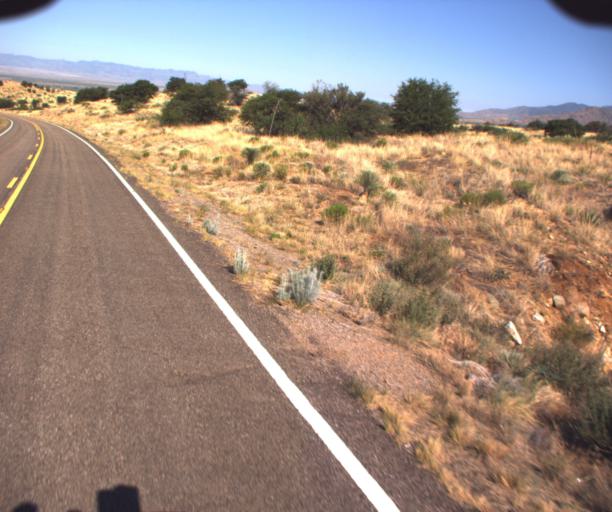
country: US
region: Arizona
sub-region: Graham County
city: Swift Trail Junction
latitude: 32.6004
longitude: -109.8870
